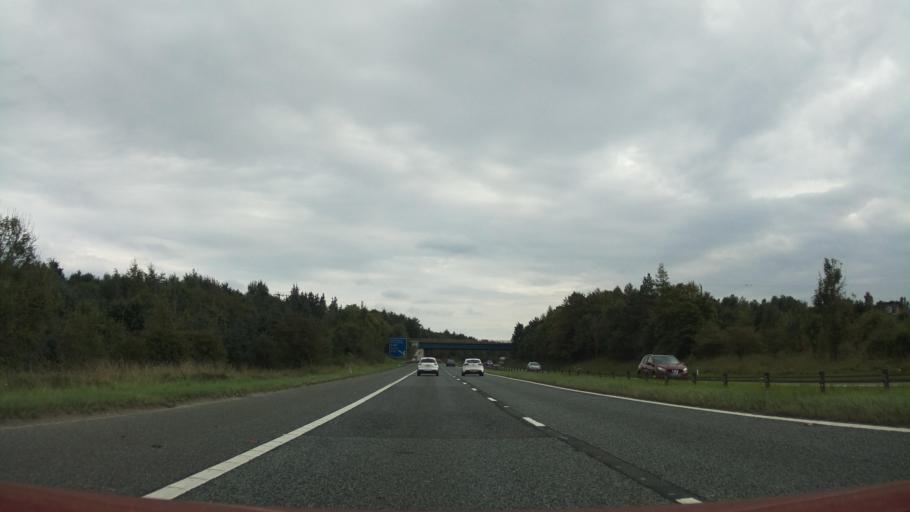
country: GB
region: England
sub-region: County Durham
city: Coxhoe
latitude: 54.7442
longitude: -1.5166
